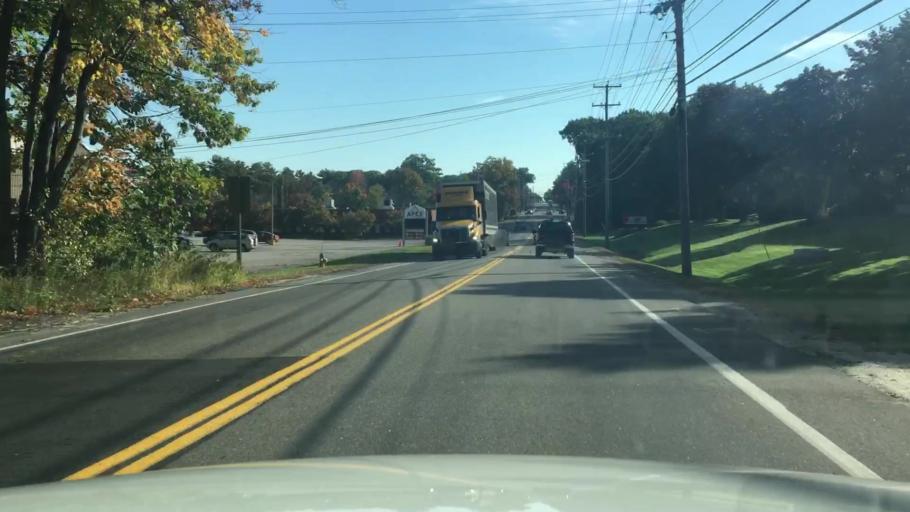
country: US
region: Maine
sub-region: Cumberland County
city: South Portland Gardens
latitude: 43.6506
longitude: -70.3413
